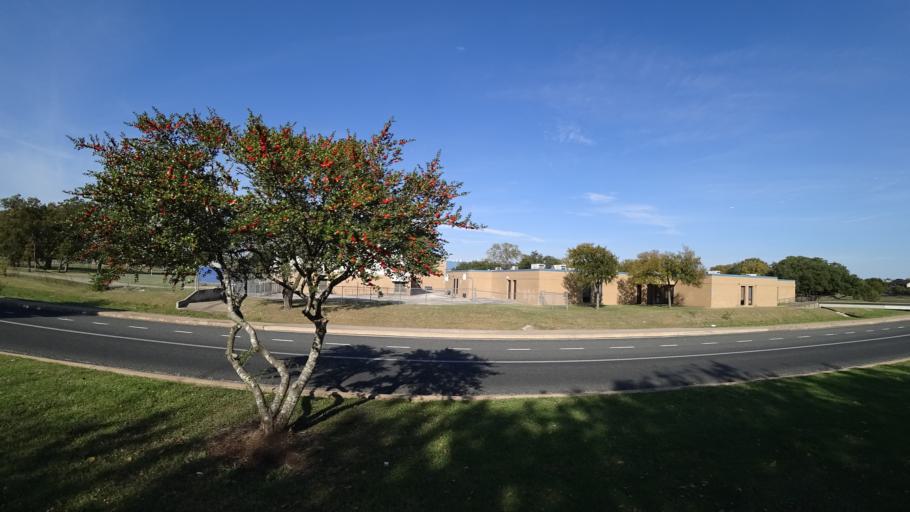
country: US
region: Texas
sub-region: Williamson County
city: Anderson Mill
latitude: 30.4560
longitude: -97.8076
